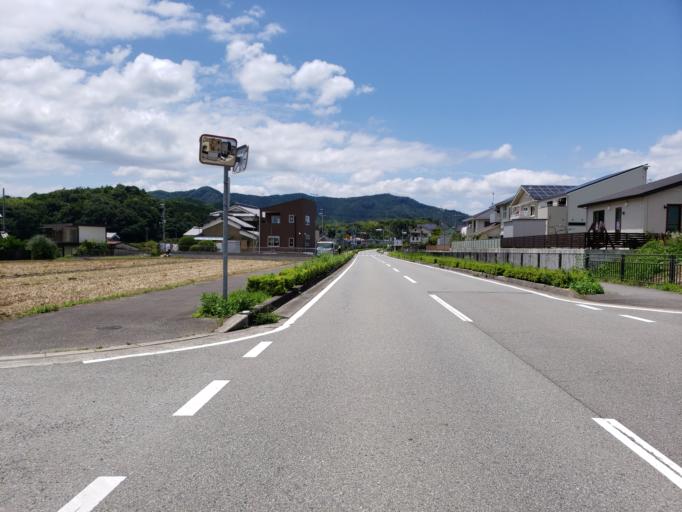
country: JP
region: Hyogo
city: Himeji
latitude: 34.9286
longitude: 134.7354
